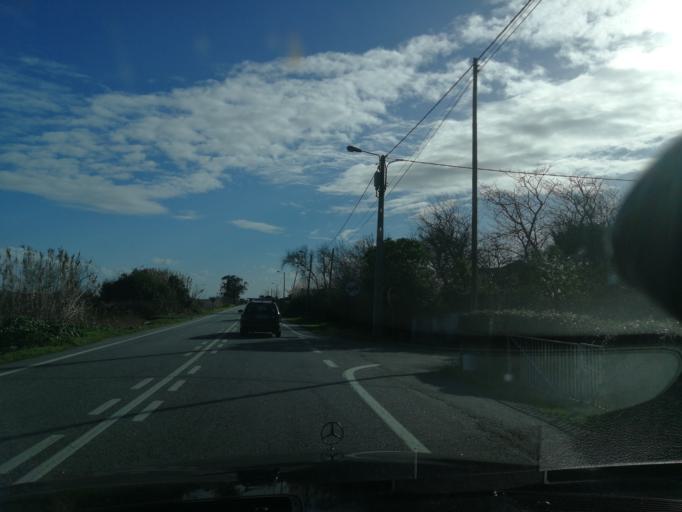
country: PT
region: Aveiro
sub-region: Estarreja
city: Pardilho
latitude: 40.7999
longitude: -8.6745
